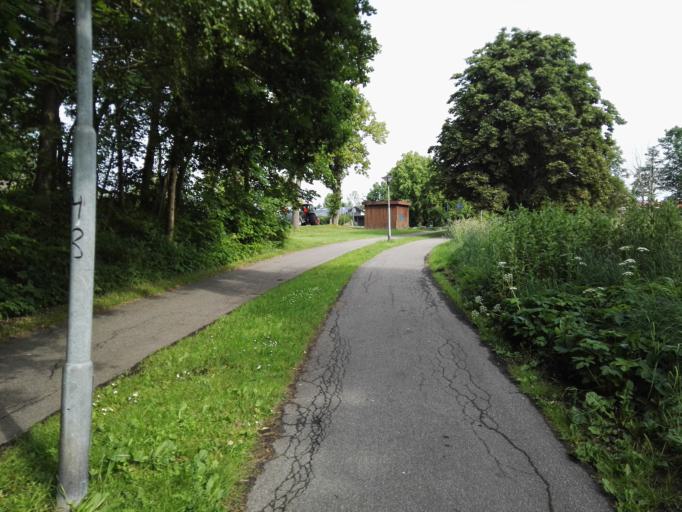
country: DK
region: Capital Region
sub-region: Egedal Kommune
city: Olstykke
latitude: 55.7849
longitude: 12.1466
